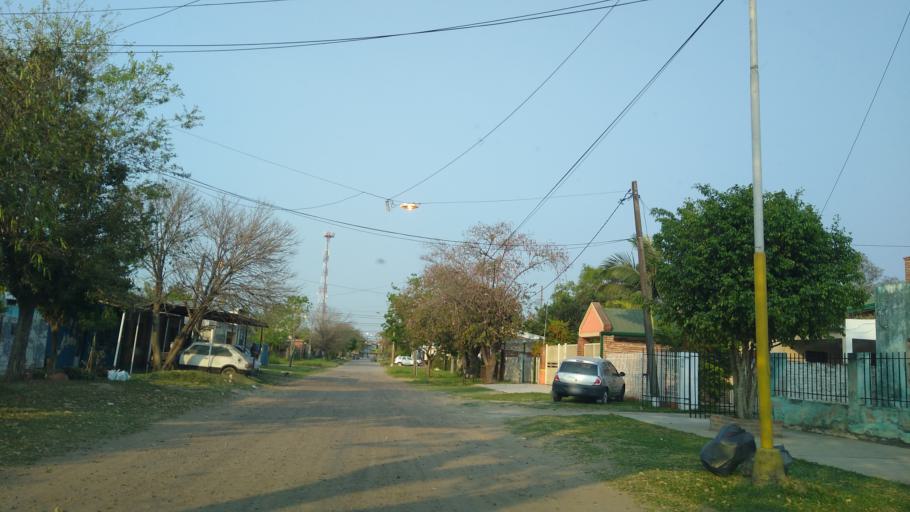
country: AR
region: Chaco
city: Barranqueras
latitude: -27.4811
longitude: -58.9394
